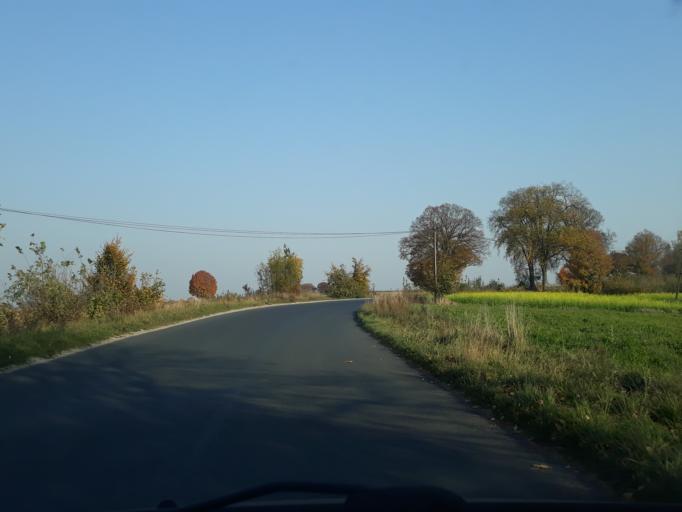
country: PL
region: Kujawsko-Pomorskie
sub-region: Powiat sepolenski
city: Sepolno Krajenskie
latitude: 53.4746
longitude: 17.4679
